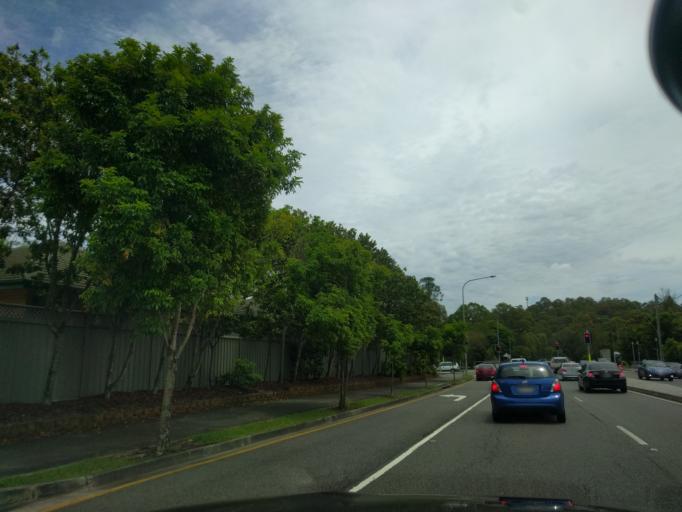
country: AU
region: Queensland
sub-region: Brisbane
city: Stafford
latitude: -27.4190
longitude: 152.9996
